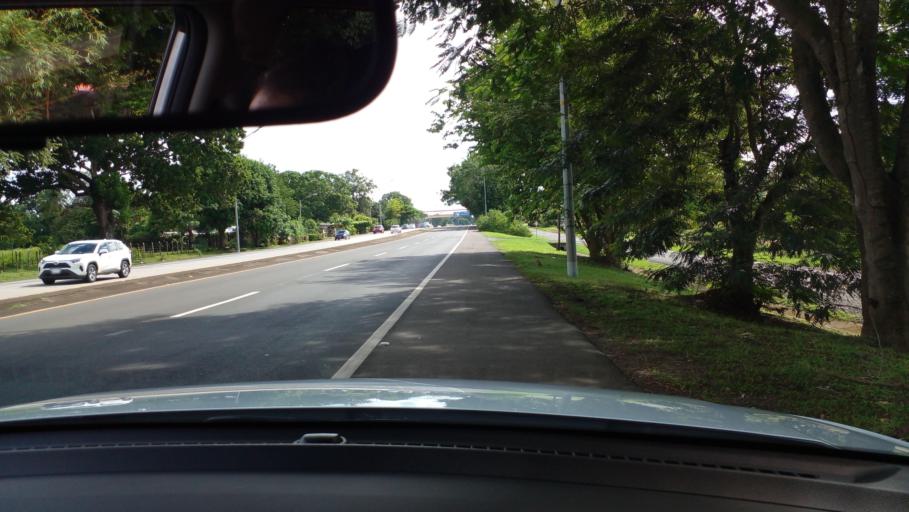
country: PA
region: Herrera
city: Santa Maria
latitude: 8.1229
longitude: -80.7022
